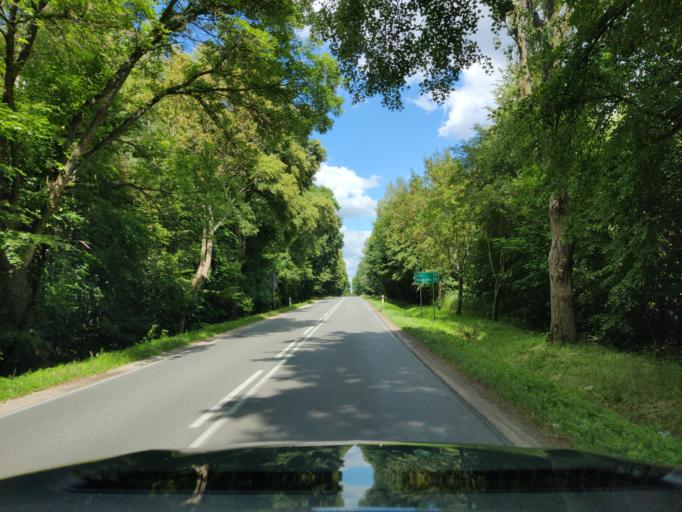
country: PL
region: Masovian Voivodeship
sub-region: Powiat minski
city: Kaluszyn
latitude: 52.2110
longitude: 21.8624
